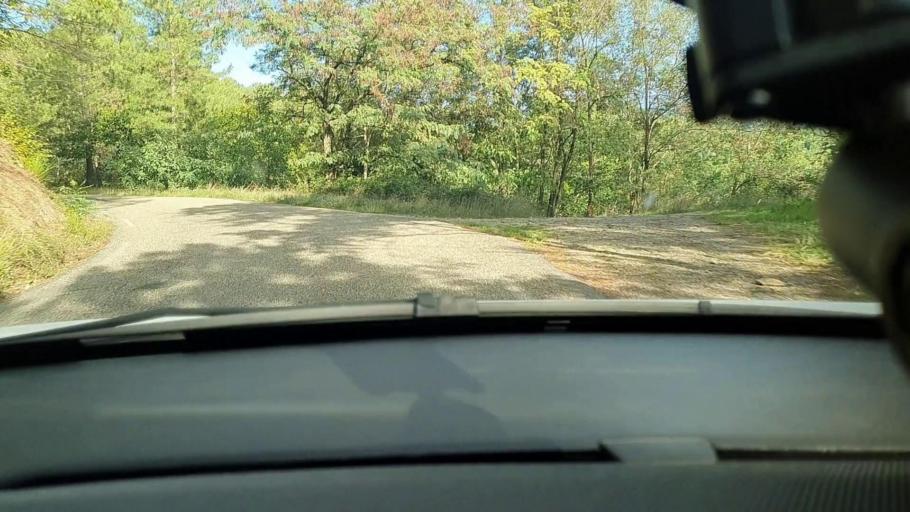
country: FR
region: Languedoc-Roussillon
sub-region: Departement du Gard
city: Besseges
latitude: 44.3213
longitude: 4.0441
